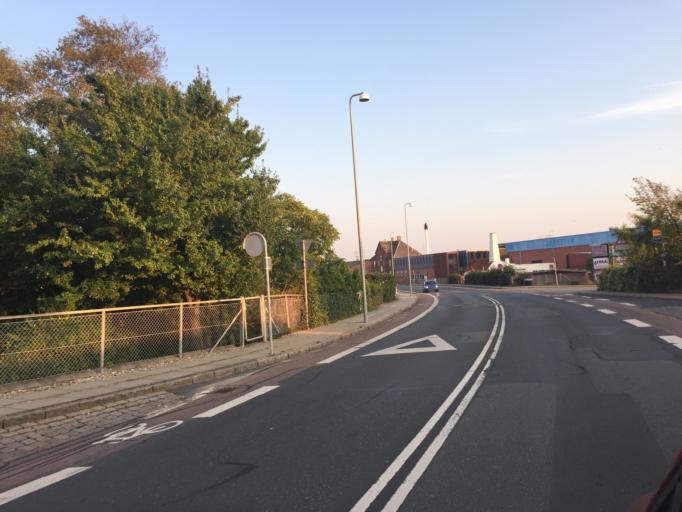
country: DK
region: South Denmark
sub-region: Faaborg-Midtfyn Kommune
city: Faaborg
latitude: 55.0977
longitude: 10.2363
